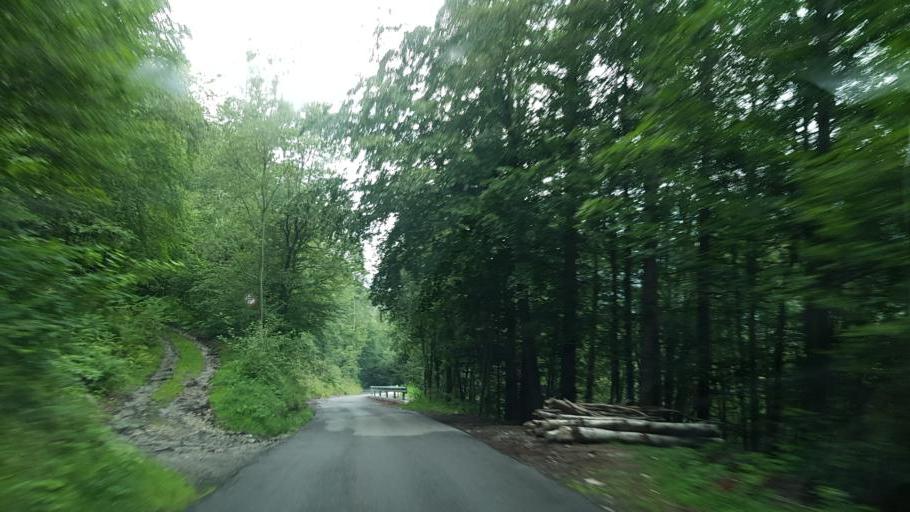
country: IT
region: Piedmont
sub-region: Provincia di Cuneo
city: Sampeyre
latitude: 44.5749
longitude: 7.1696
